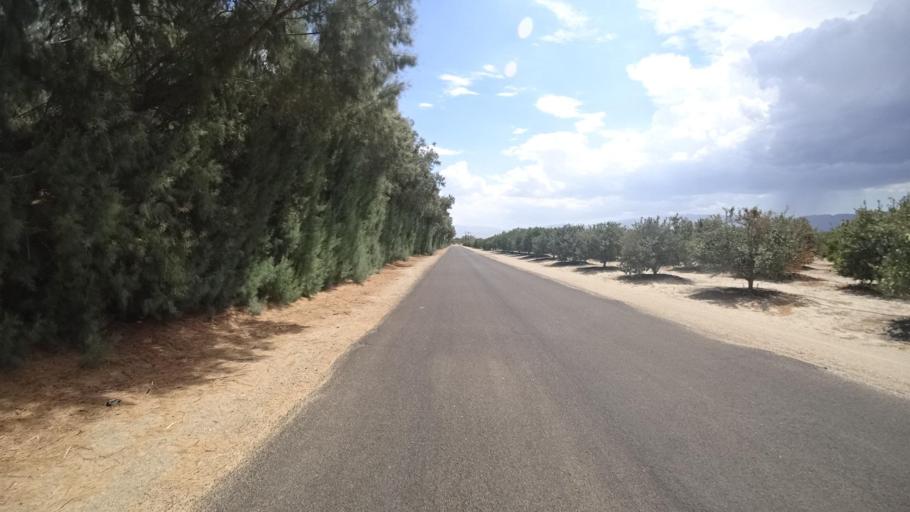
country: US
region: California
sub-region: San Diego County
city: Borrego Springs
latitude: 33.3036
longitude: -116.3494
